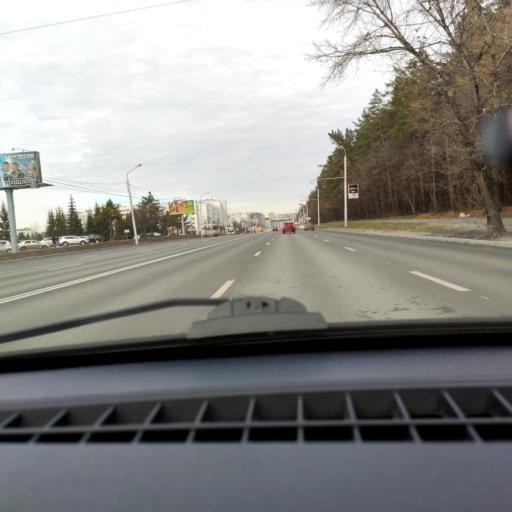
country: RU
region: Bashkortostan
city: Ufa
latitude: 54.7415
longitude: 56.0287
